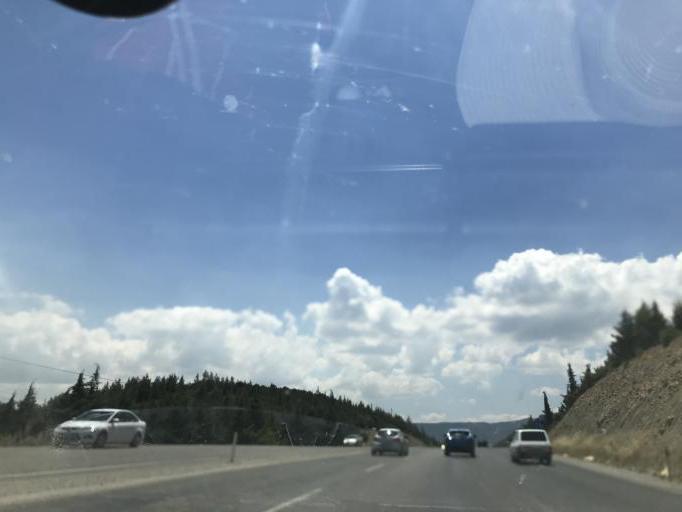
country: TR
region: Denizli
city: Honaz
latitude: 37.7054
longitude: 29.2041
